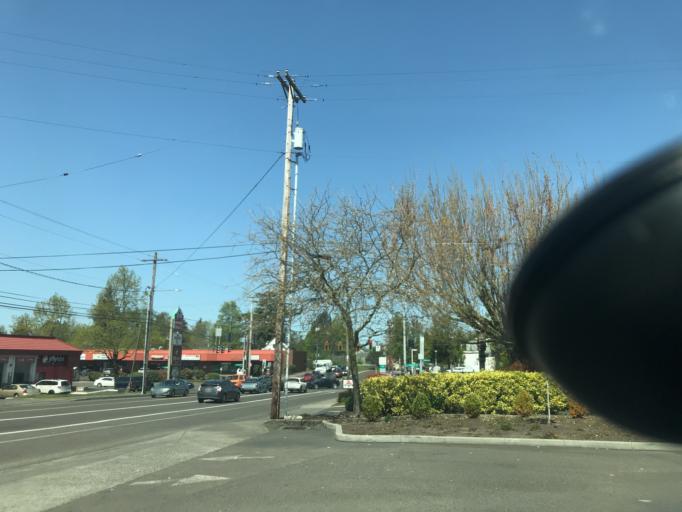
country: US
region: Oregon
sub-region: Multnomah County
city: Lents
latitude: 45.4966
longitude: -122.5683
